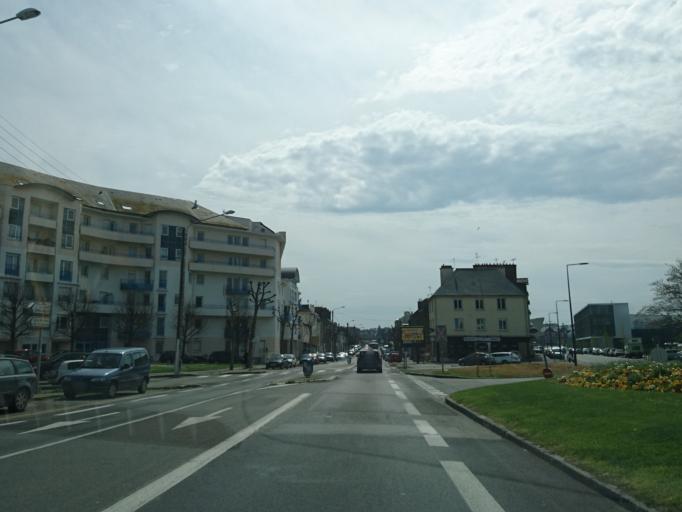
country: FR
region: Brittany
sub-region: Departement d'Ille-et-Vilaine
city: Saint-Malo
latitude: 48.6444
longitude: -2.0084
